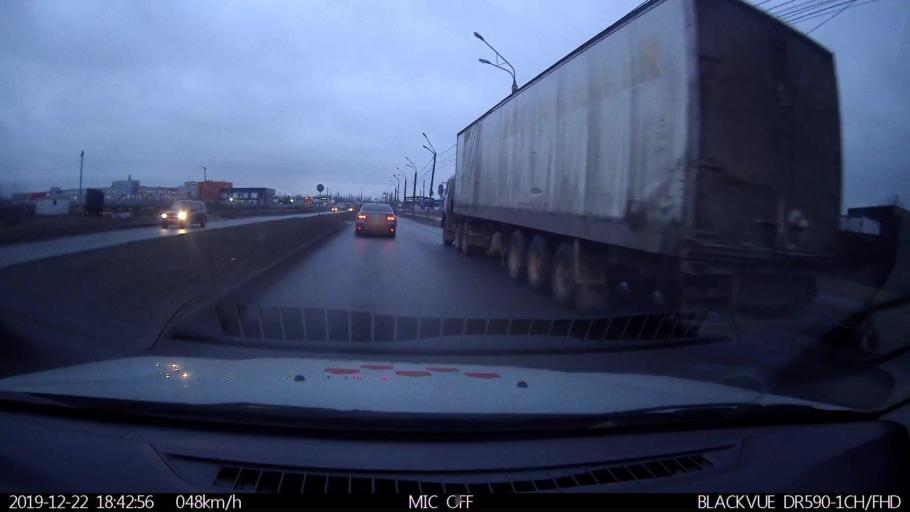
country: RU
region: Nizjnij Novgorod
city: Neklyudovo
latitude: 56.3432
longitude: 43.8889
